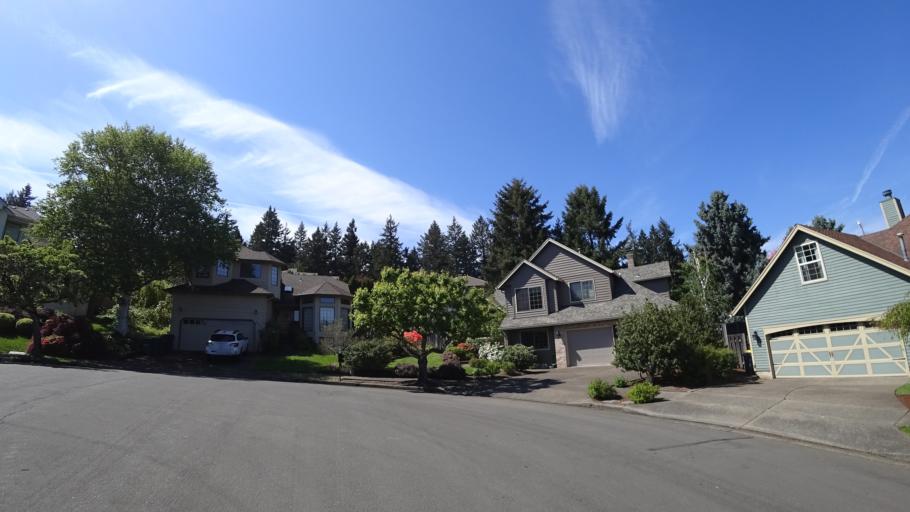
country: US
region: Oregon
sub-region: Washington County
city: Aloha
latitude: 45.4490
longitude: -122.8435
